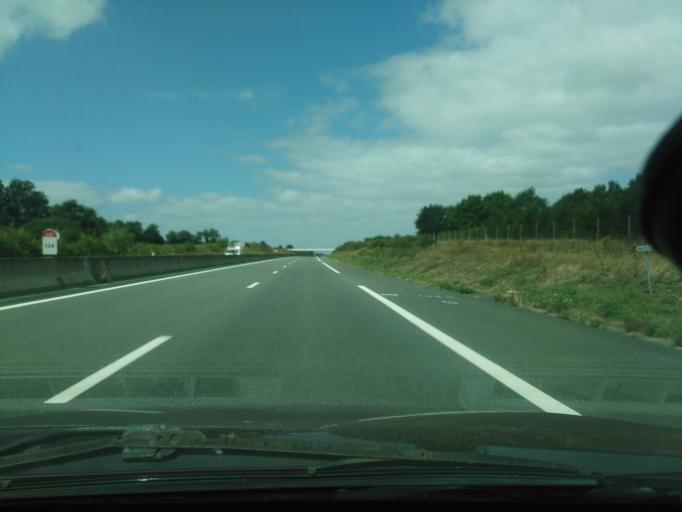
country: FR
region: Pays de la Loire
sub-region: Departement de la Vendee
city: Les Clouzeaux
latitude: 46.6317
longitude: -1.4716
